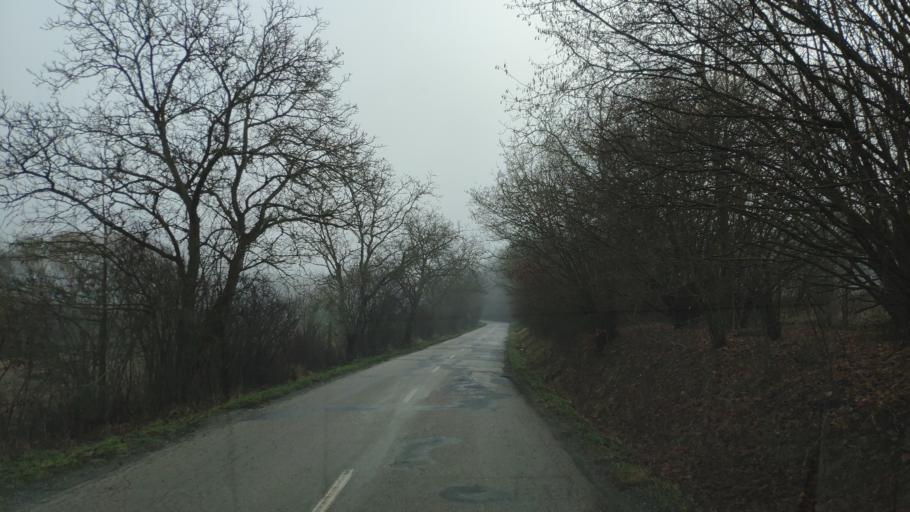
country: SK
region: Kosicky
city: Kosice
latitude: 48.7122
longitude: 21.3689
